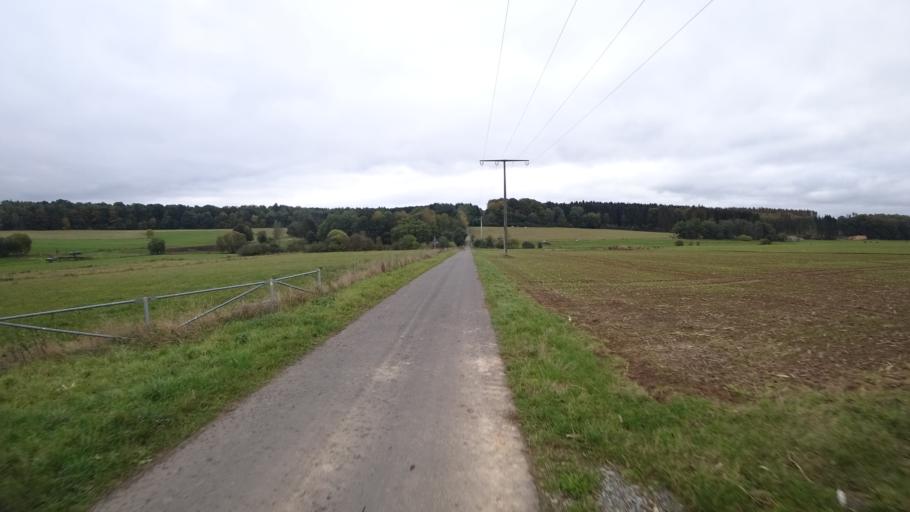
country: DE
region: Rheinland-Pfalz
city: Marienrachdorf
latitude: 50.5457
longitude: 7.7101
